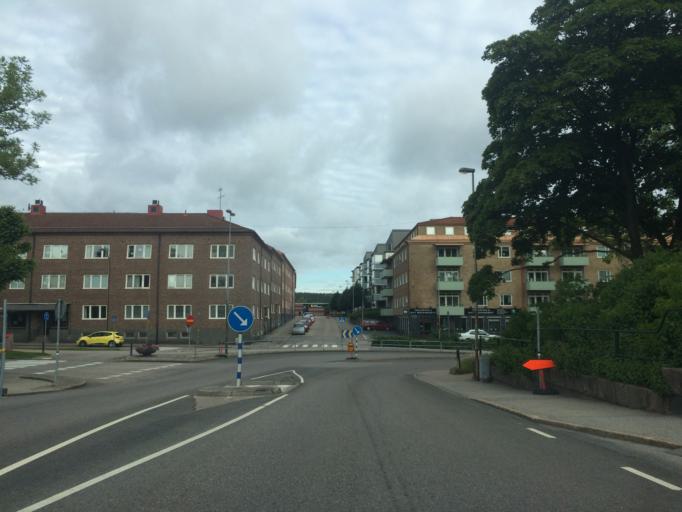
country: SE
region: Vaestra Goetaland
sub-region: Trollhattan
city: Trollhattan
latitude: 58.2880
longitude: 12.2963
